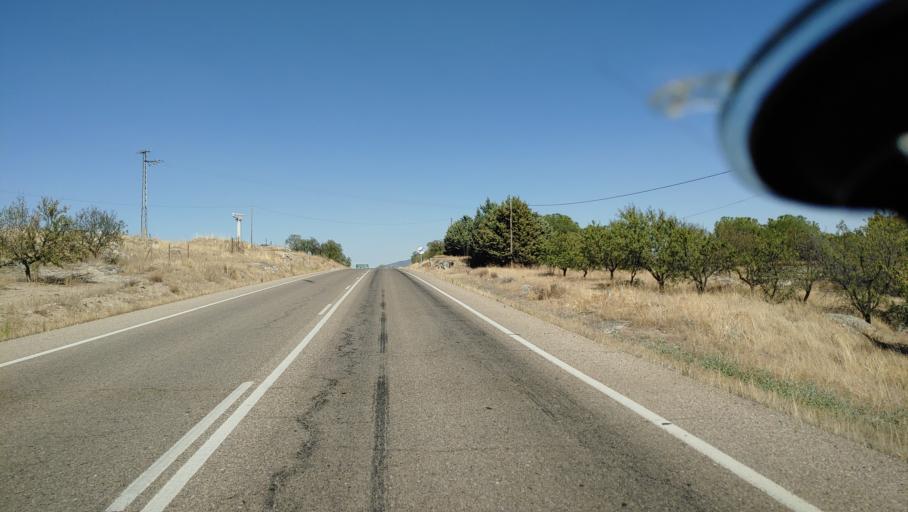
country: ES
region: Castille-La Mancha
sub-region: Province of Toledo
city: Cuerva
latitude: 39.6691
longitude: -4.1998
